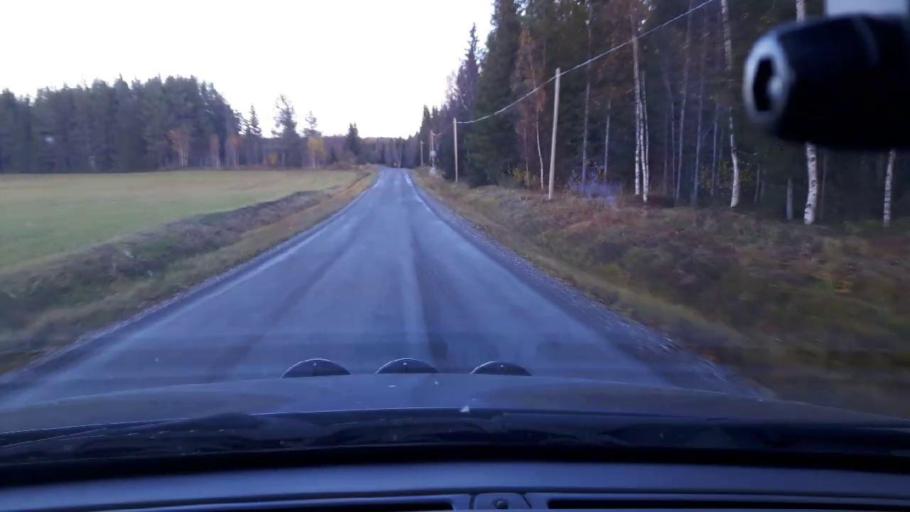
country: SE
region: Jaemtland
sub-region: Bergs Kommun
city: Hoverberg
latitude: 63.0649
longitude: 14.2609
